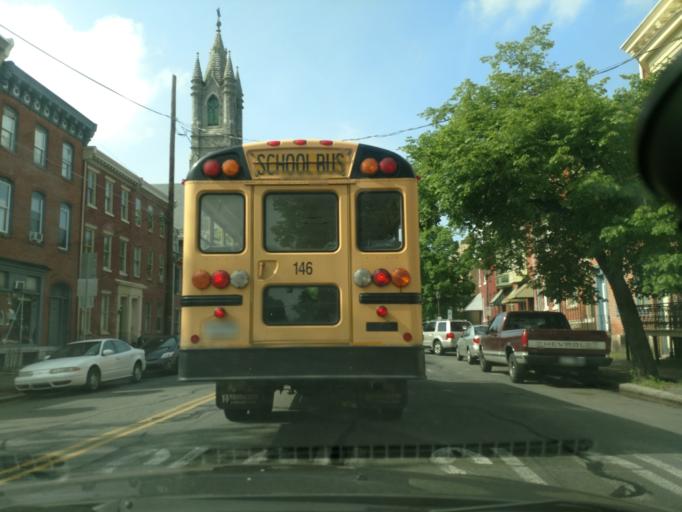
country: US
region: Pennsylvania
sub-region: Berks County
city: Reading
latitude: 40.3292
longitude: -75.9281
